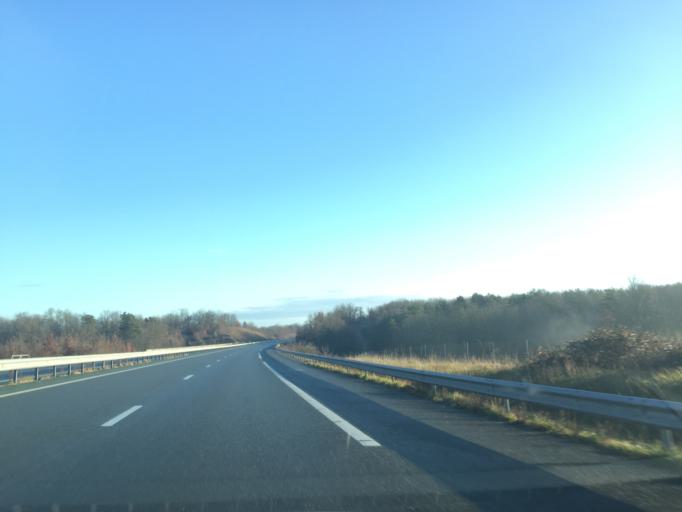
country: FR
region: Aquitaine
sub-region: Departement de la Dordogne
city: Thenon
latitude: 45.1744
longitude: 0.9607
